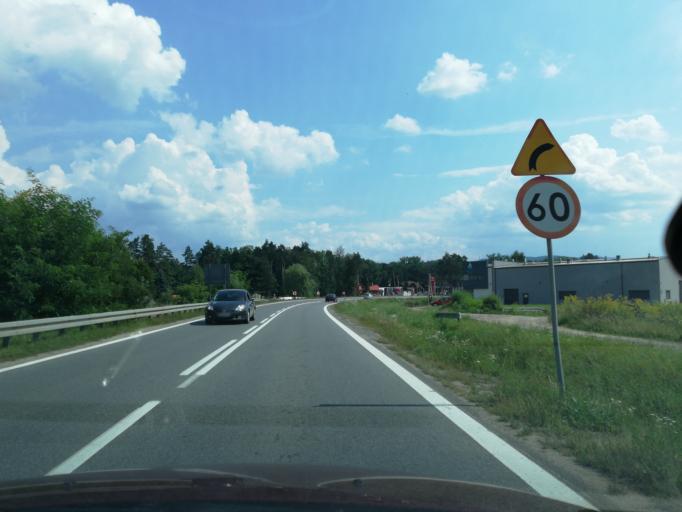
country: PL
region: Lesser Poland Voivodeship
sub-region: Powiat nowosadecki
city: Stary Sacz
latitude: 49.5700
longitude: 20.6542
